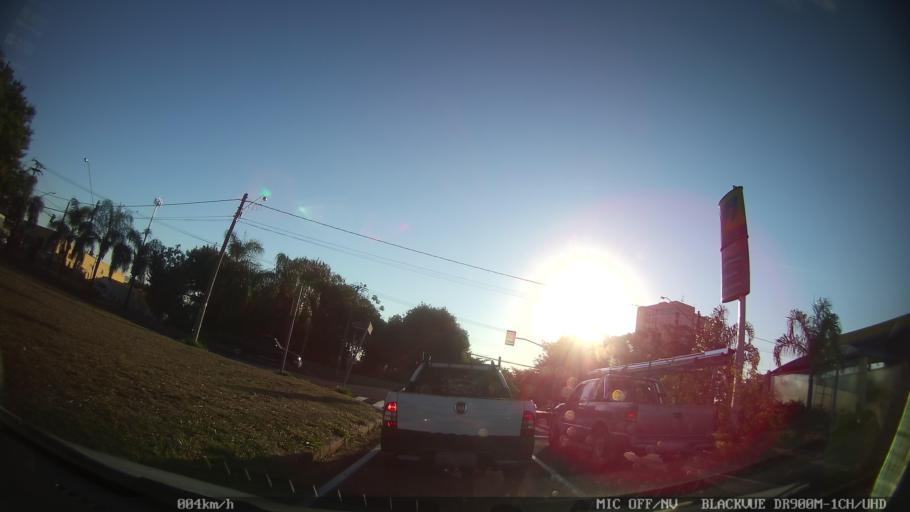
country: BR
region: Sao Paulo
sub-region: Sao Jose Do Rio Preto
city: Sao Jose do Rio Preto
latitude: -20.7868
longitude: -49.3682
